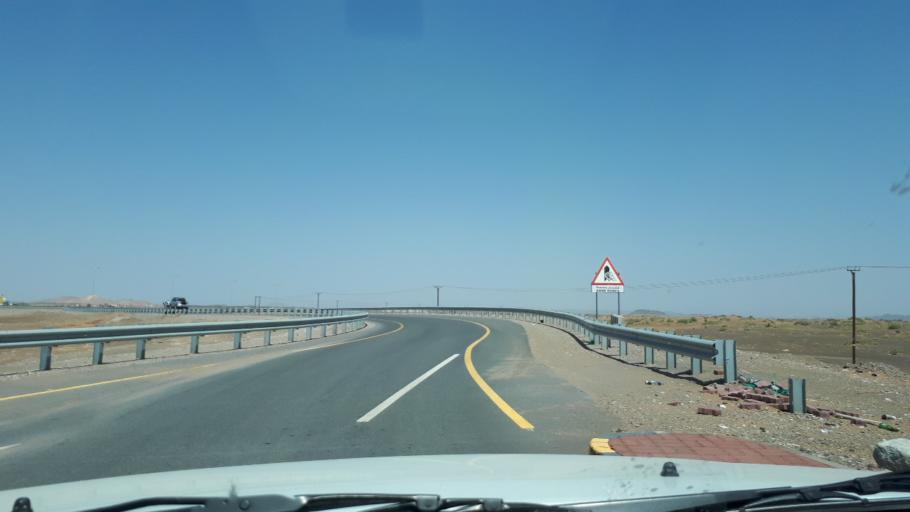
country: OM
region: Ash Sharqiyah
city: Al Qabil
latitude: 22.5248
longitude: 58.7429
